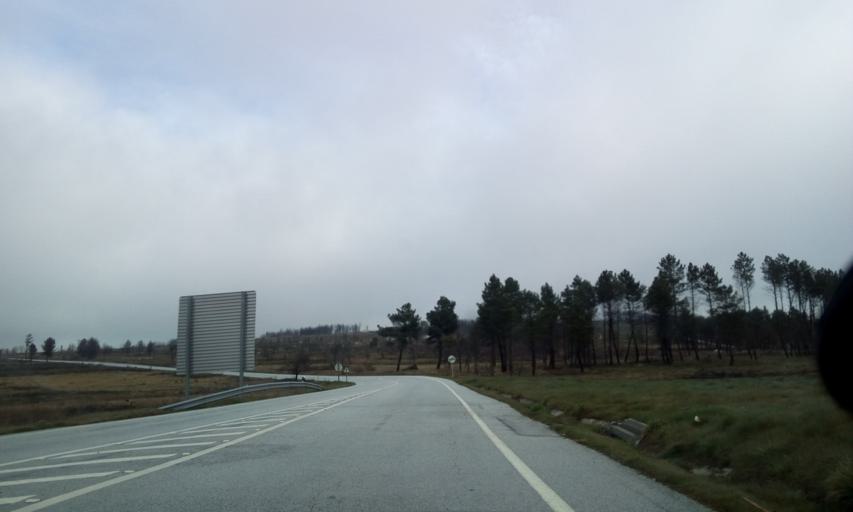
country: PT
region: Guarda
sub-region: Fornos de Algodres
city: Fornos de Algodres
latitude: 40.6969
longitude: -7.4738
